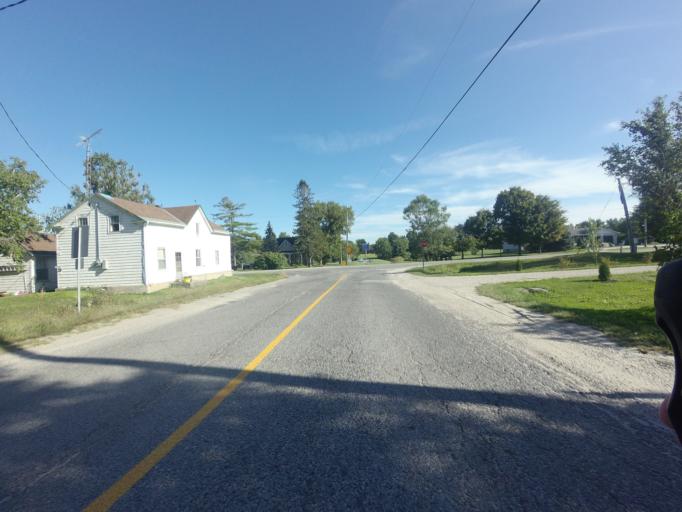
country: CA
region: Ontario
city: Perth
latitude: 44.8828
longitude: -76.3093
